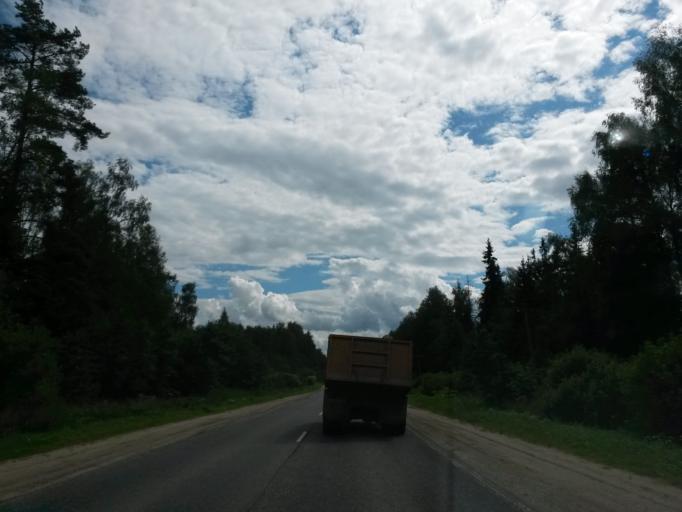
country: RU
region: Ivanovo
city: Novo-Talitsy
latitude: 57.0492
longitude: 40.7369
